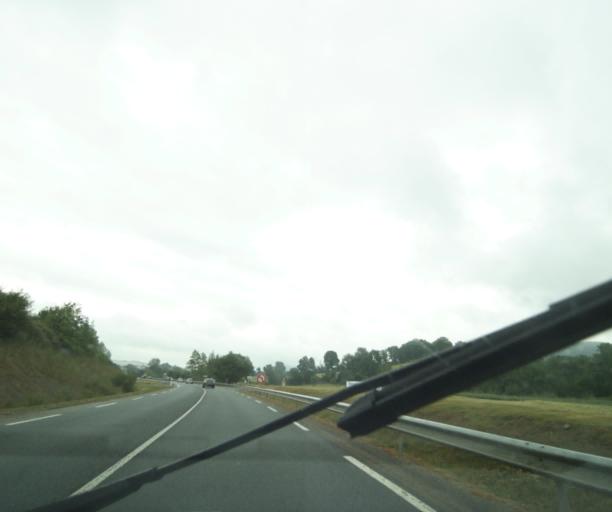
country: FR
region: Midi-Pyrenees
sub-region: Departement de l'Aveyron
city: Laissac
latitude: 44.3844
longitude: 2.8015
